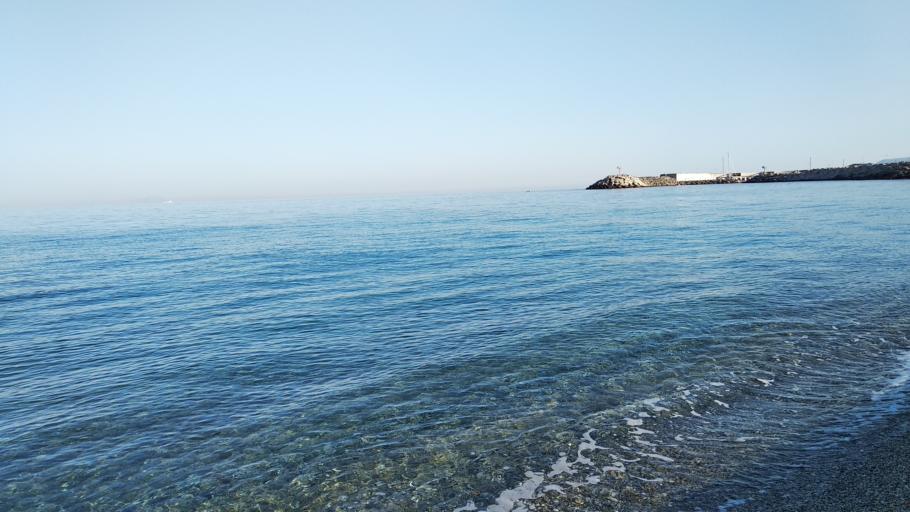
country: IT
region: Calabria
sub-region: Provincia di Reggio Calabria
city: Palmi
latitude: 38.3859
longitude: 15.8619
